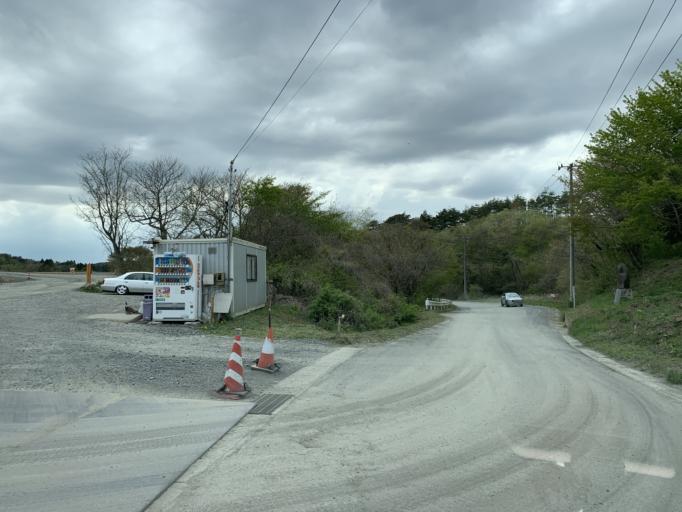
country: JP
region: Iwate
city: Ichinoseki
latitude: 38.7931
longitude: 141.4166
